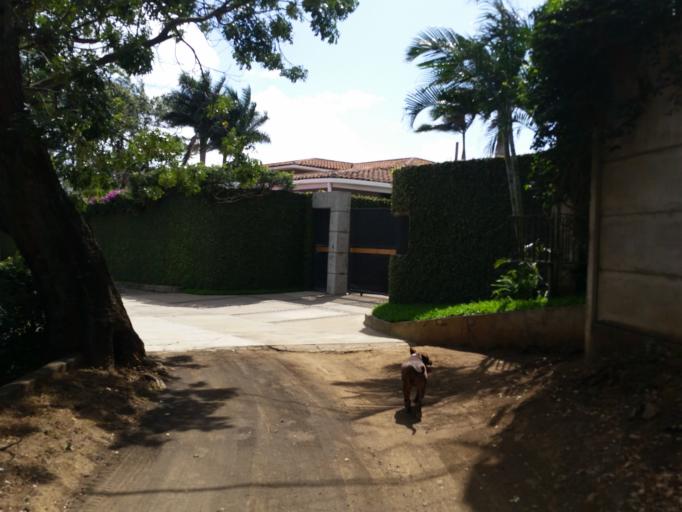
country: NI
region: Managua
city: Managua
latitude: 12.0825
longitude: -86.2499
